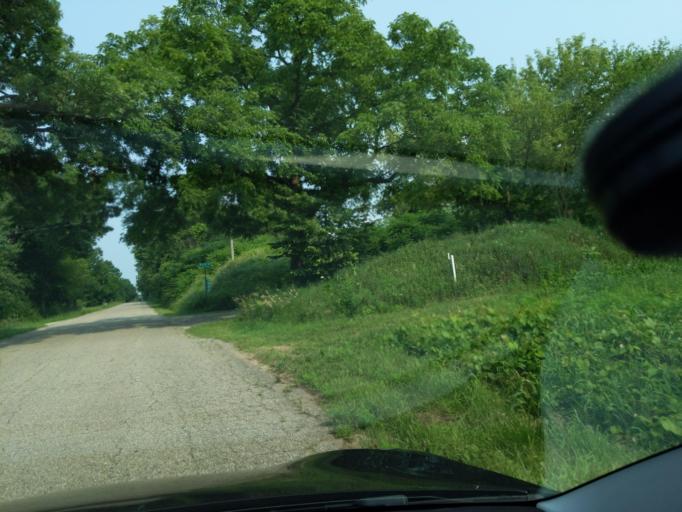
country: US
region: Michigan
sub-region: Eaton County
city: Eaton Rapids
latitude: 42.4220
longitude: -84.5726
